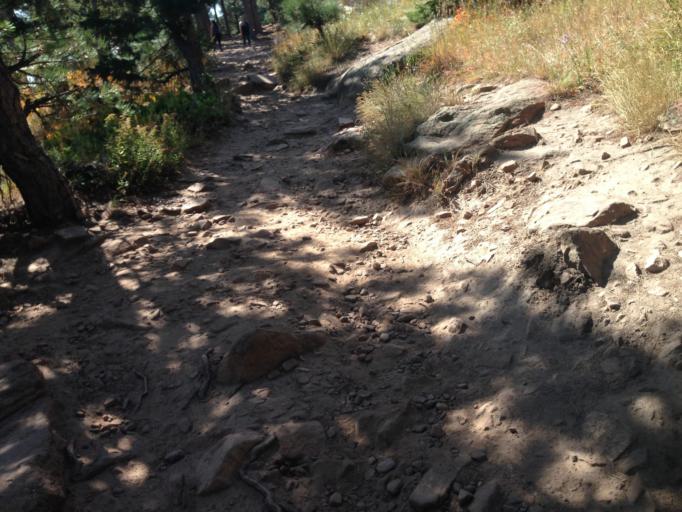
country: US
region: Colorado
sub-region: Boulder County
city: Boulder
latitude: 39.9924
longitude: -105.2892
